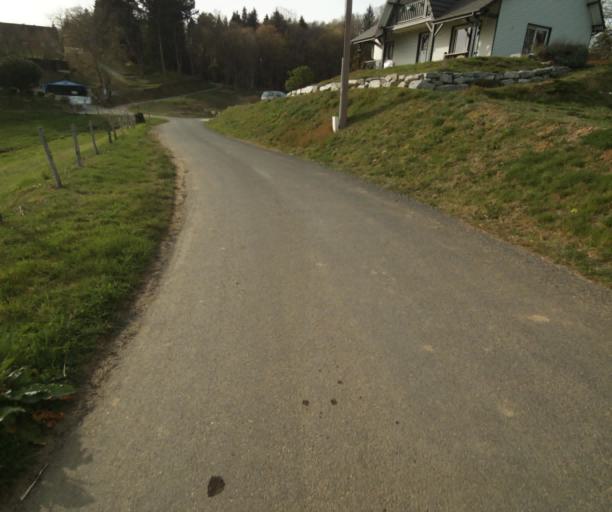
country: FR
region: Limousin
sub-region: Departement de la Correze
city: Naves
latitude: 45.3232
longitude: 1.7577
